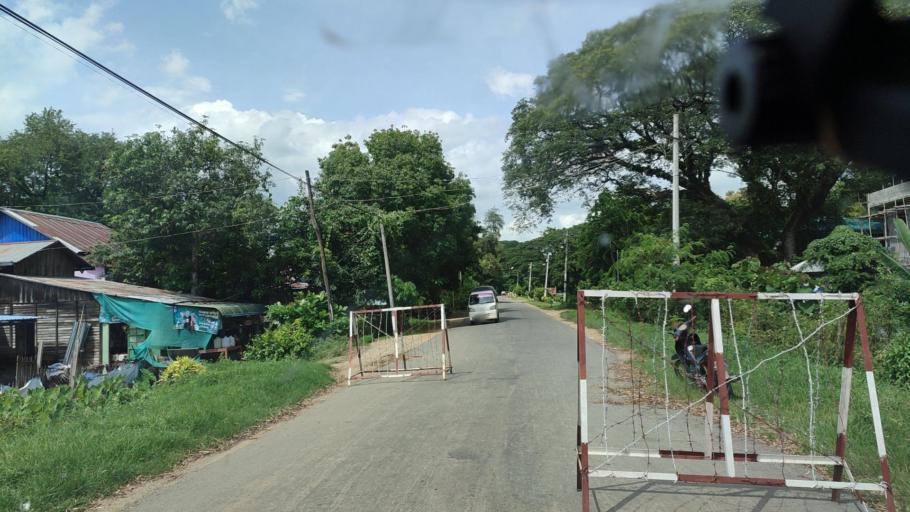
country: MM
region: Bago
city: Pyay
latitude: 18.7182
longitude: 95.1594
